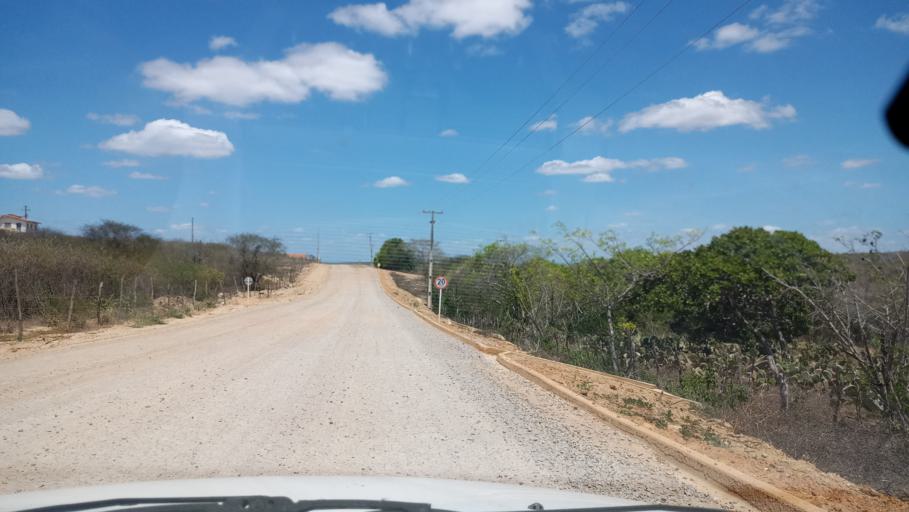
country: BR
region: Rio Grande do Norte
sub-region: Sao Paulo Do Potengi
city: Sao Paulo do Potengi
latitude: -5.7751
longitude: -35.9137
